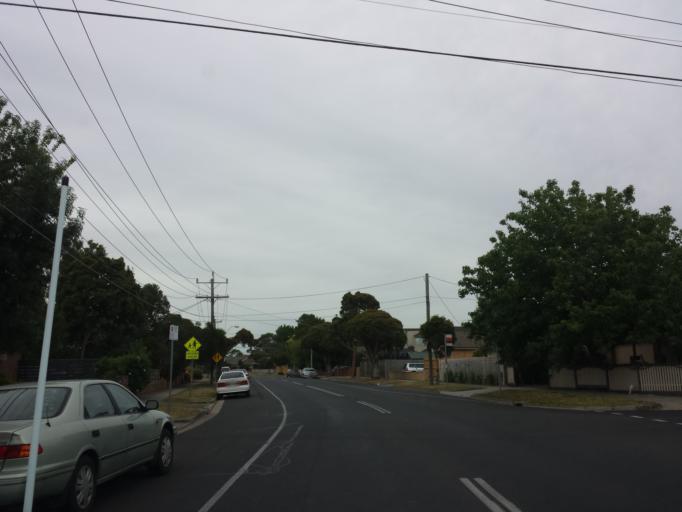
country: AU
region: Victoria
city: Highett
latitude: -37.9397
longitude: 145.0542
